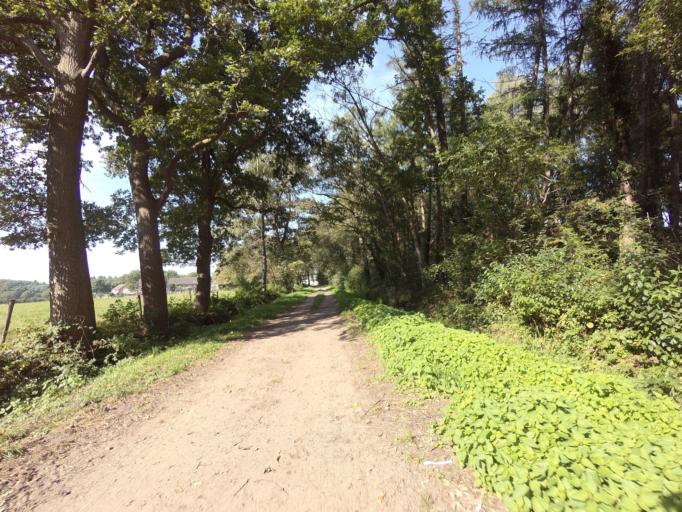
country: NL
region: Overijssel
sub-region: Gemeente Enschede
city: Enschede
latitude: 52.1889
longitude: 6.9119
